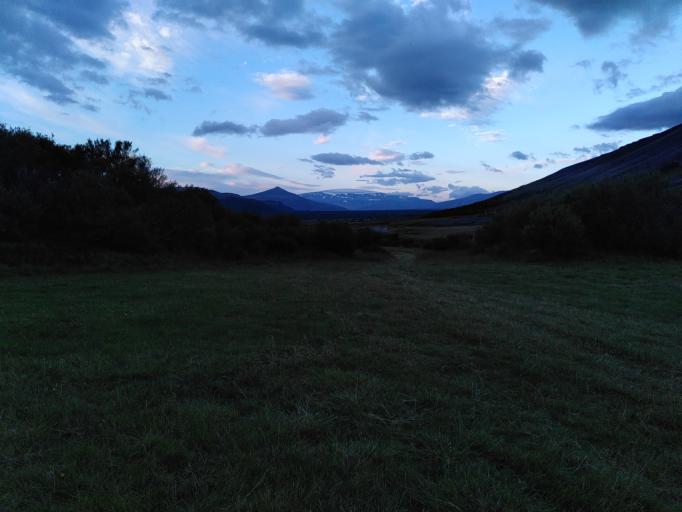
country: IS
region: South
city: Hveragerdi
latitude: 64.6942
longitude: -20.9445
